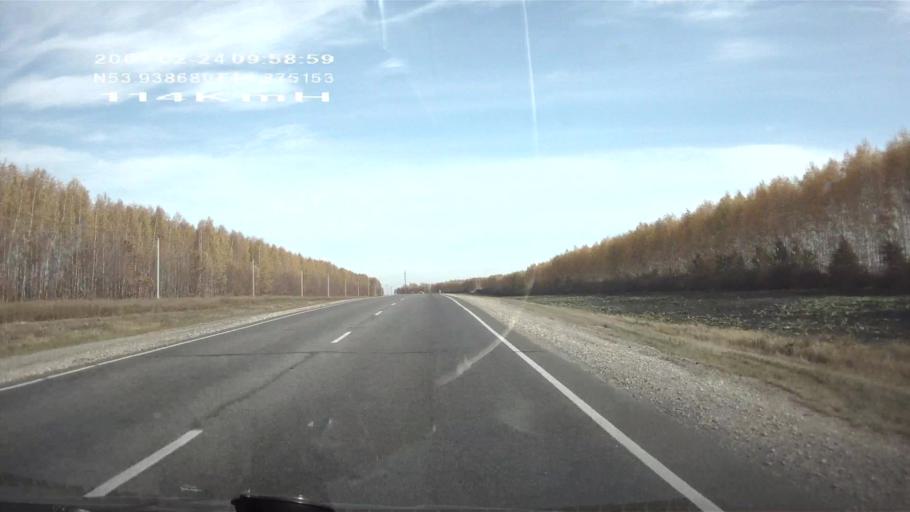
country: RU
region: Penza
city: Issa
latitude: 53.9390
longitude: 44.8755
